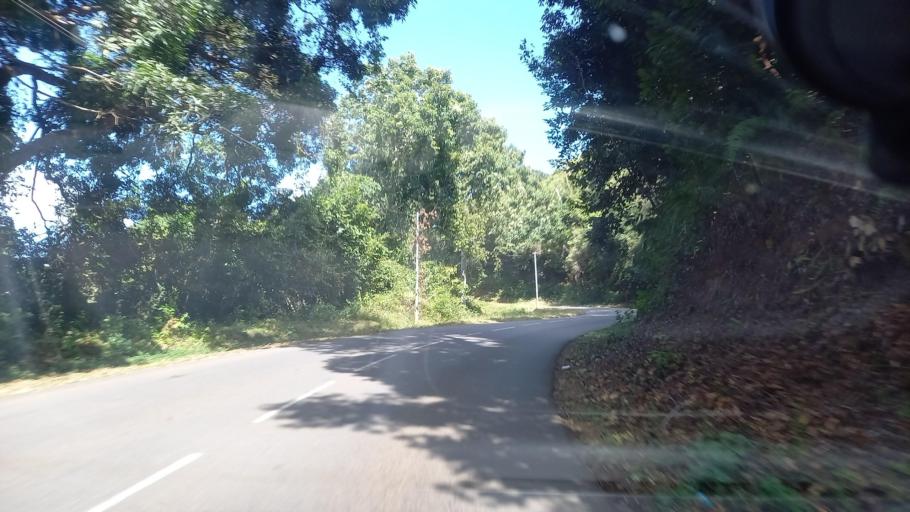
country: YT
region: Dembeni
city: Dembeni
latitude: -12.7865
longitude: 45.1659
